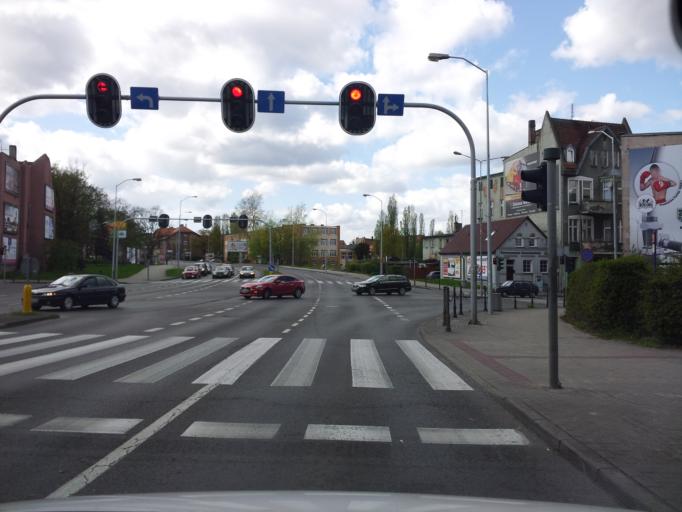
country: PL
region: Lubusz
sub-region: Zielona Gora
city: Zielona Gora
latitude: 51.9359
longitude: 15.5024
